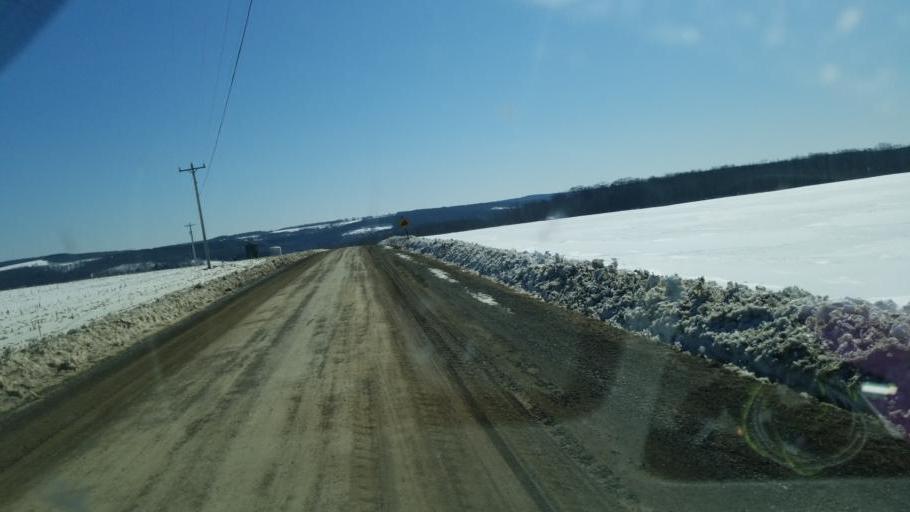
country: US
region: New York
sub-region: Allegany County
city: Andover
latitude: 42.0941
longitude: -77.6771
